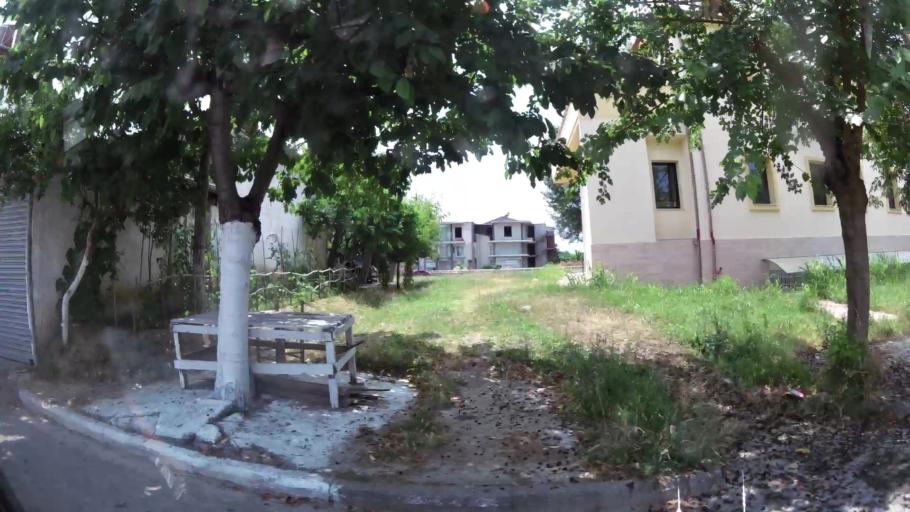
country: GR
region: Central Macedonia
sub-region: Nomos Pierias
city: Peristasi
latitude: 40.2731
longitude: 22.5379
